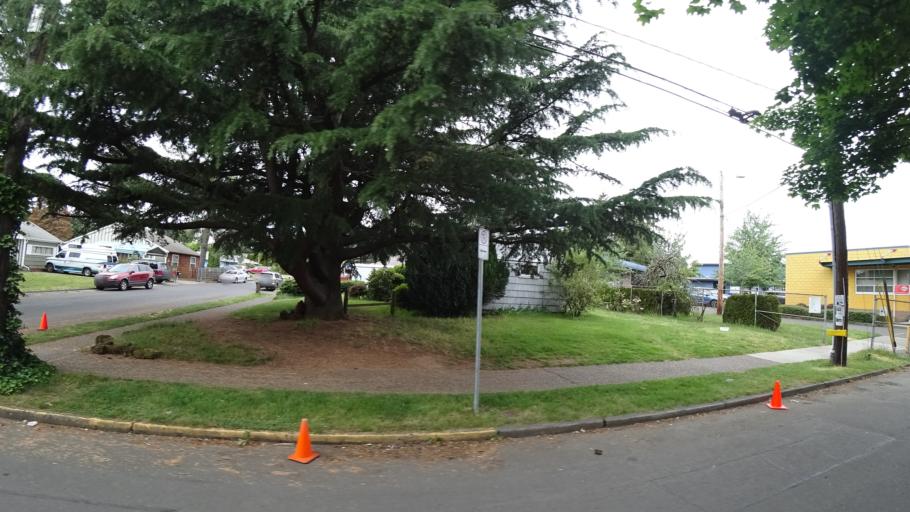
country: US
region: Oregon
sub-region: Multnomah County
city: Lents
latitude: 45.5003
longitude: -122.5435
